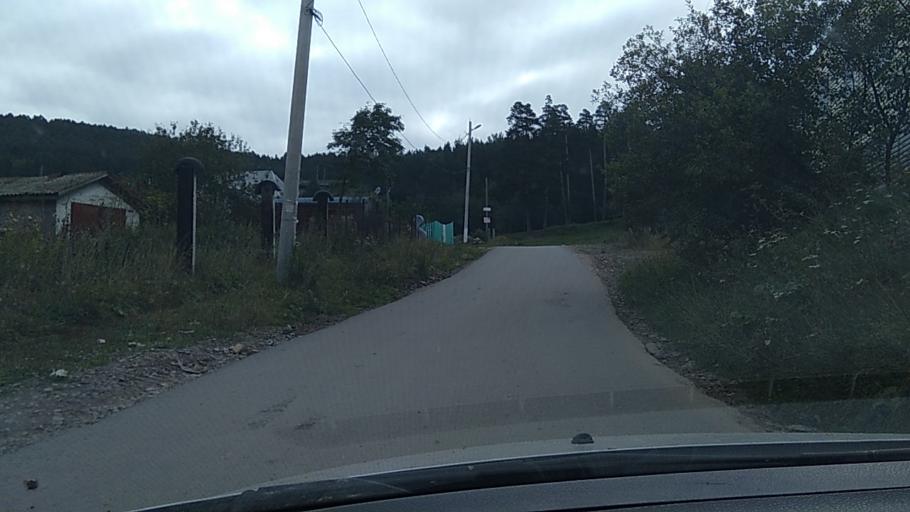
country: RU
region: Chelyabinsk
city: Zlatoust
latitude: 55.1710
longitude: 59.7080
